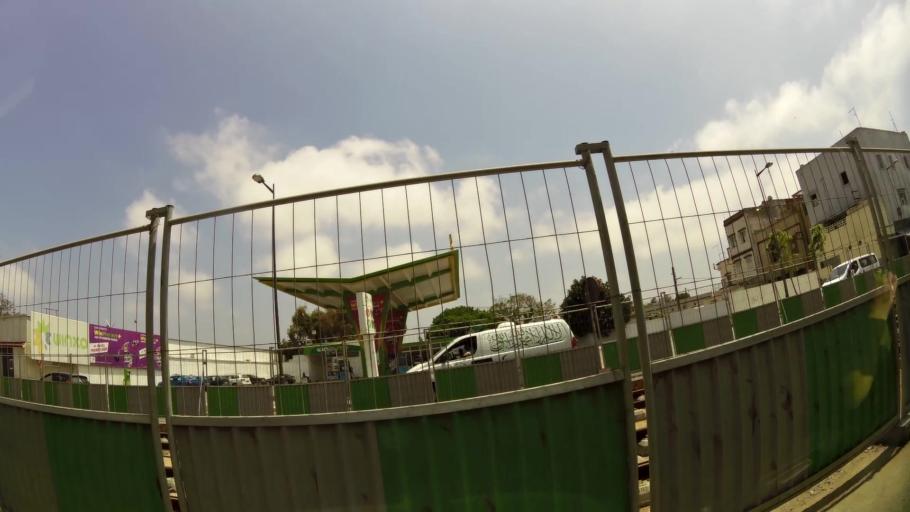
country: MA
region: Rabat-Sale-Zemmour-Zaer
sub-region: Rabat
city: Rabat
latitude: 34.0073
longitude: -6.8624
